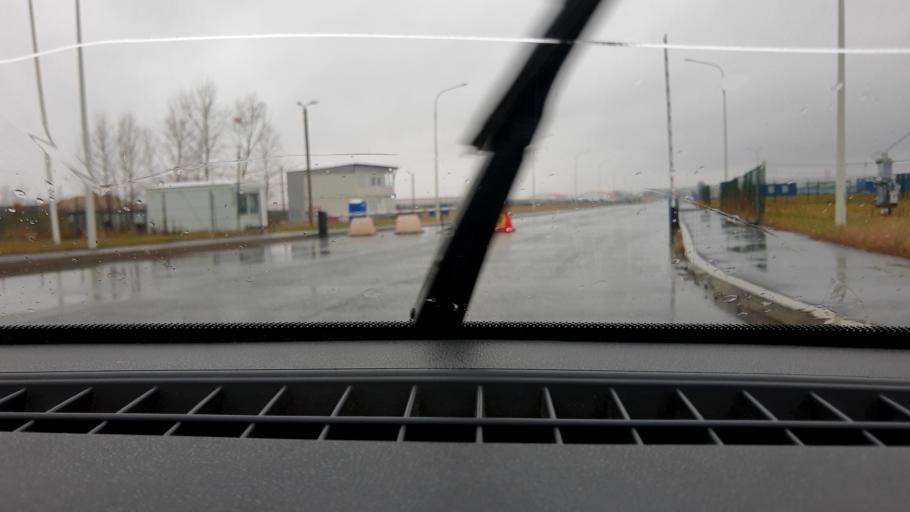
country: RU
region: Bashkortostan
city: Ufa
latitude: 54.6020
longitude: 55.9155
